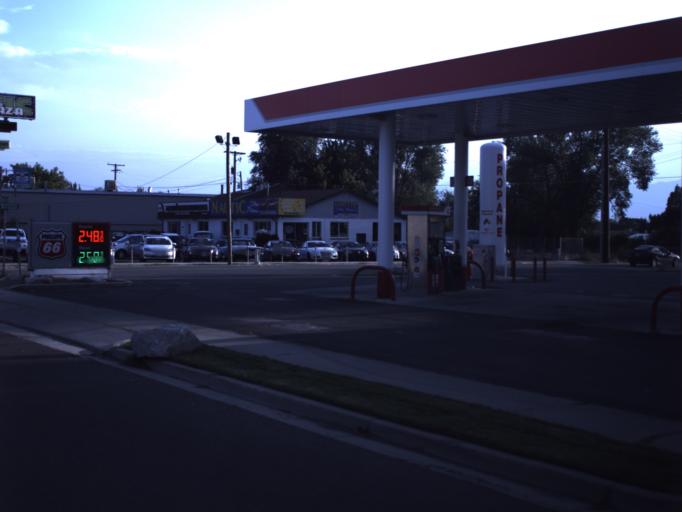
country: US
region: Utah
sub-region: Salt Lake County
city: Sandy City
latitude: 40.5993
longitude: -111.8909
